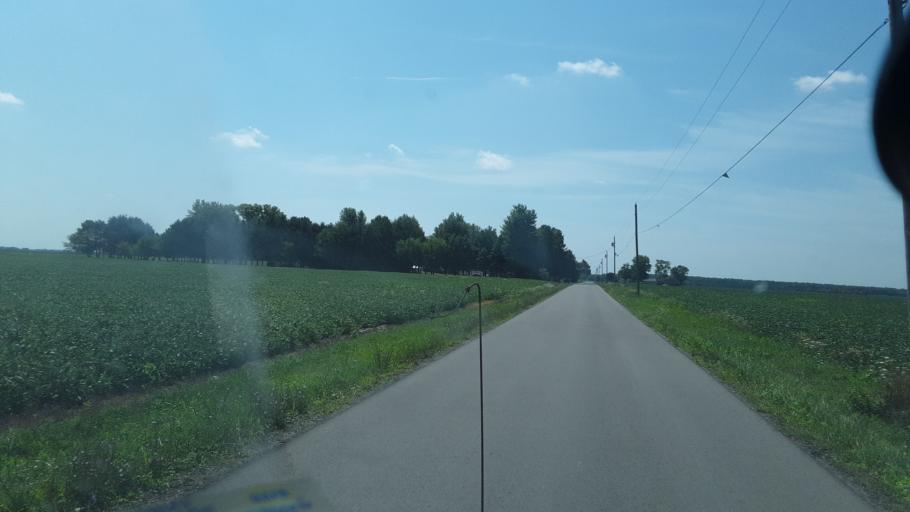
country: US
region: Ohio
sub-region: Hancock County
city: Findlay
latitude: 41.0031
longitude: -83.5161
